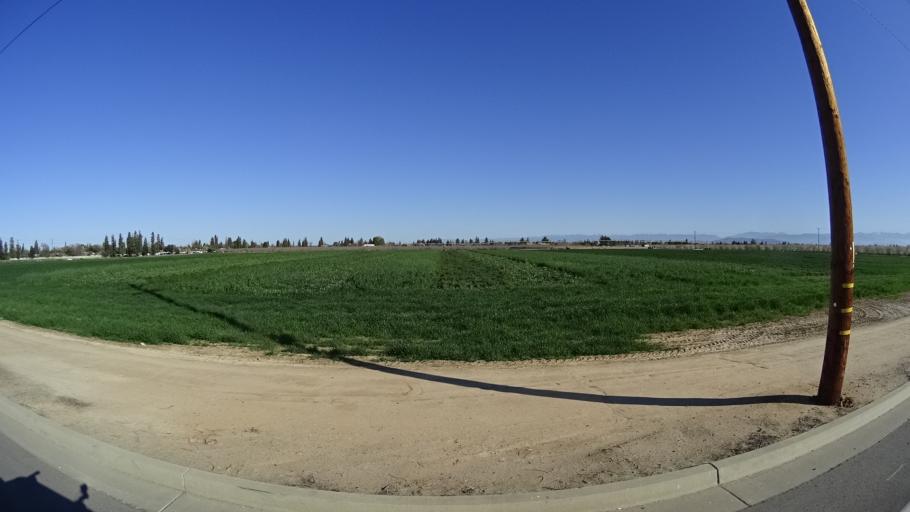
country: US
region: California
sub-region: Fresno County
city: Clovis
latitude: 36.8232
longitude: -119.7513
